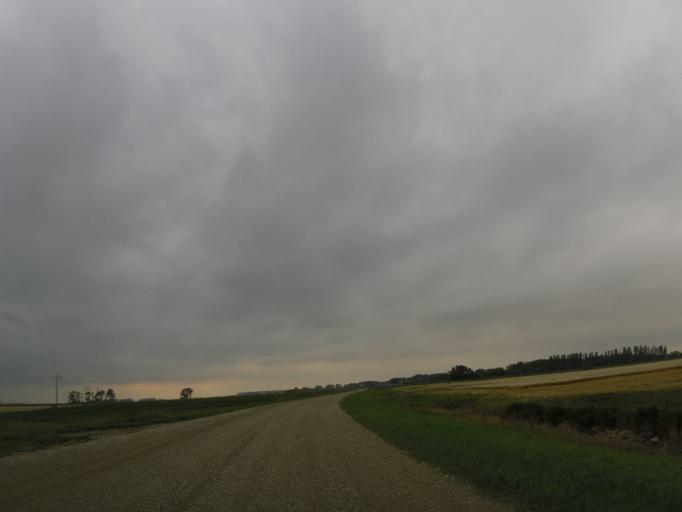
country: US
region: North Dakota
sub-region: Walsh County
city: Grafton
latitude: 48.5285
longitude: -97.1778
